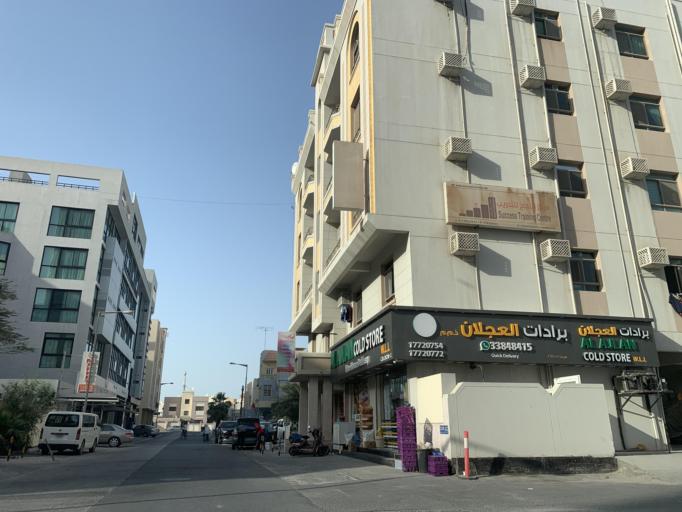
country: BH
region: Manama
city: Manama
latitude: 26.2047
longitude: 50.5813
